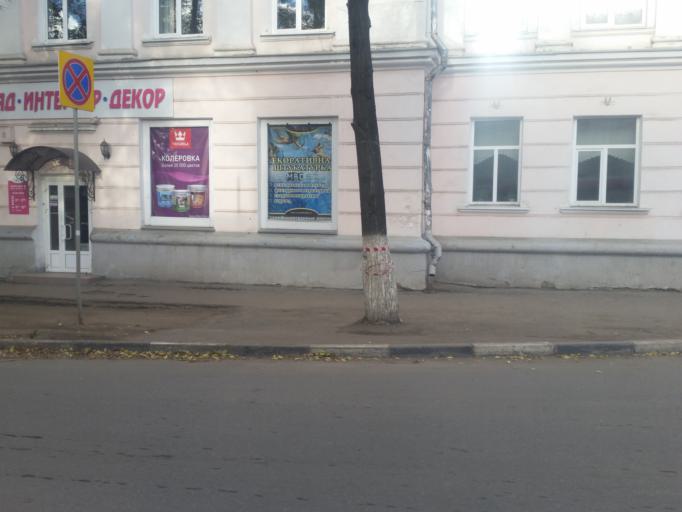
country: RU
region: Ulyanovsk
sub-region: Ulyanovskiy Rayon
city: Ulyanovsk
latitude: 54.3238
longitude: 48.3939
